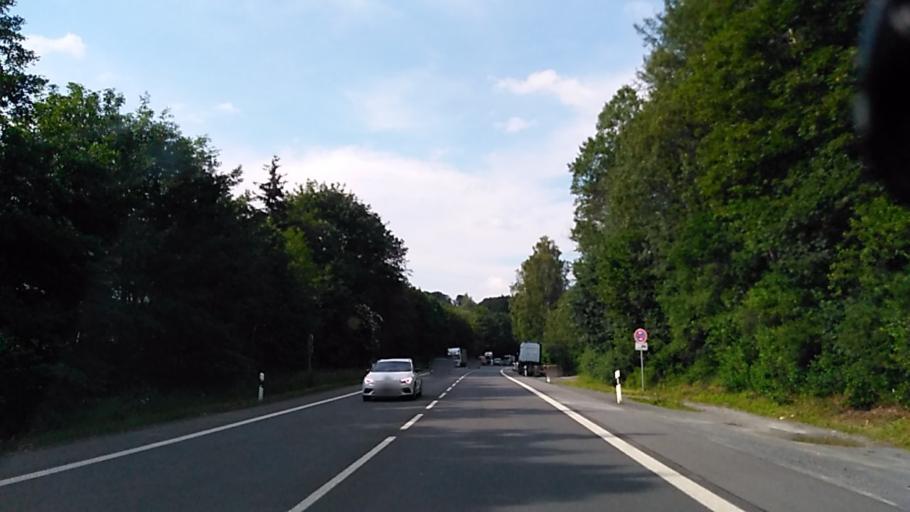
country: DE
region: North Rhine-Westphalia
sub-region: Regierungsbezirk Arnsberg
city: Luedenscheid
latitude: 51.2249
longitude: 7.6615
